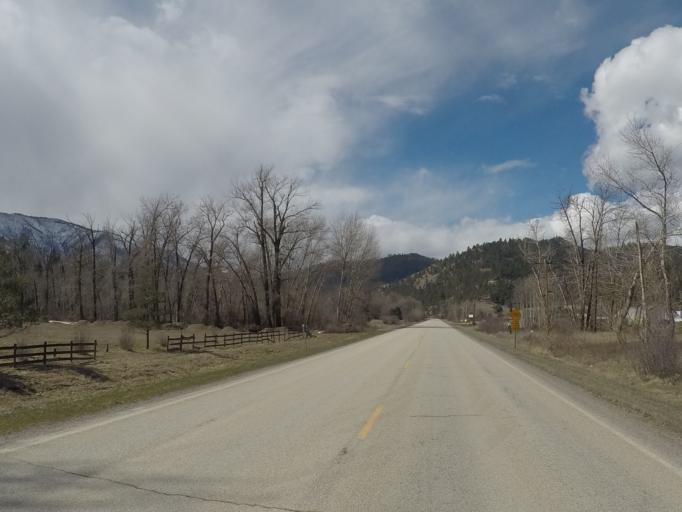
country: US
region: Montana
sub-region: Missoula County
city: Lolo
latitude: 46.7568
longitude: -114.1070
